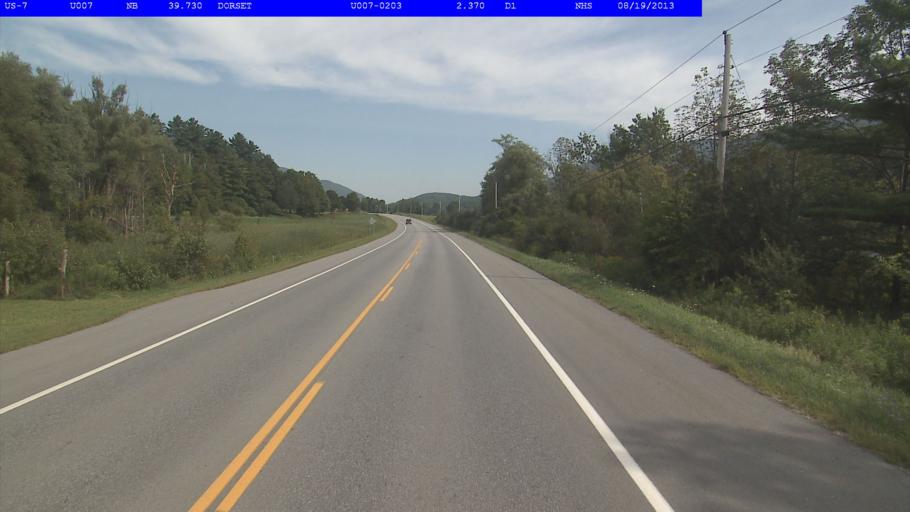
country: US
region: Vermont
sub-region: Bennington County
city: Manchester Center
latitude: 43.2431
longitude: -73.0087
